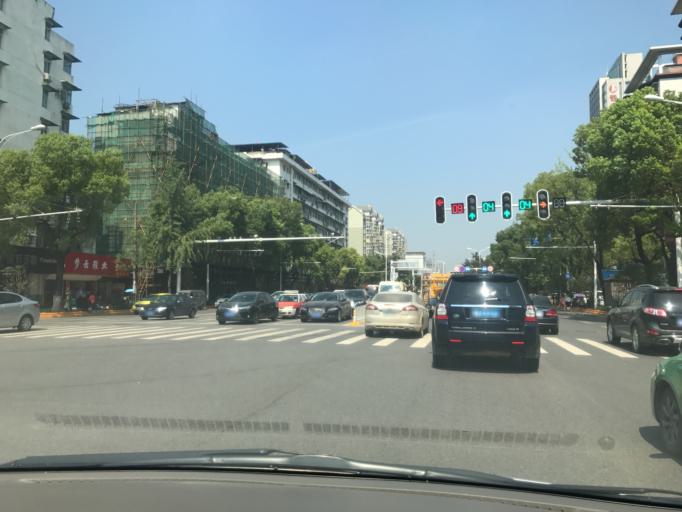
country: CN
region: Hubei
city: Yongfeng
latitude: 30.5598
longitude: 114.2221
